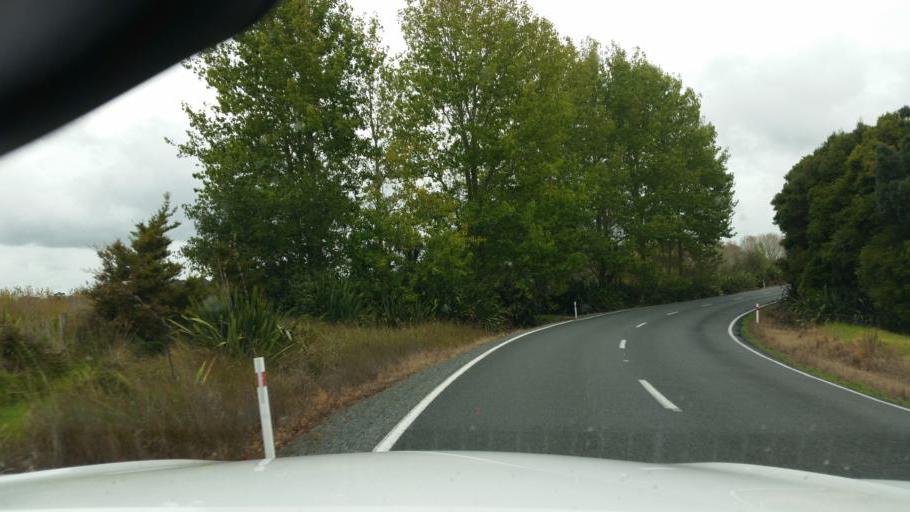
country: NZ
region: Auckland
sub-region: Auckland
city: Wellsford
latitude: -36.1459
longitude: 174.4810
